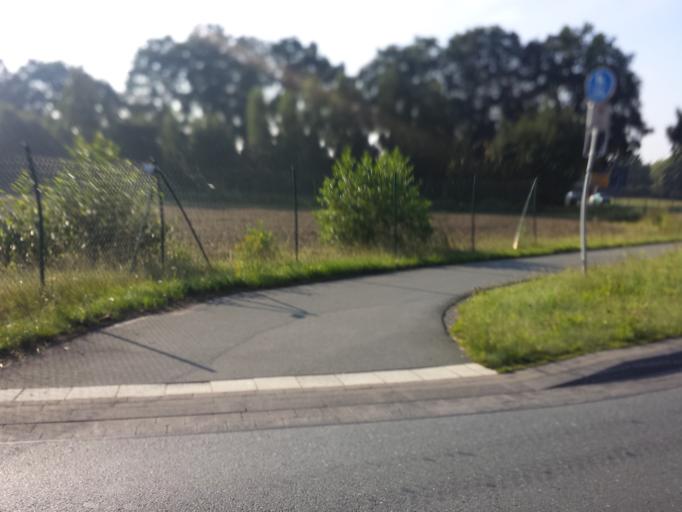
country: DE
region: North Rhine-Westphalia
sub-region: Regierungsbezirk Detmold
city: Harsewinkel
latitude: 51.9434
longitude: 8.2895
